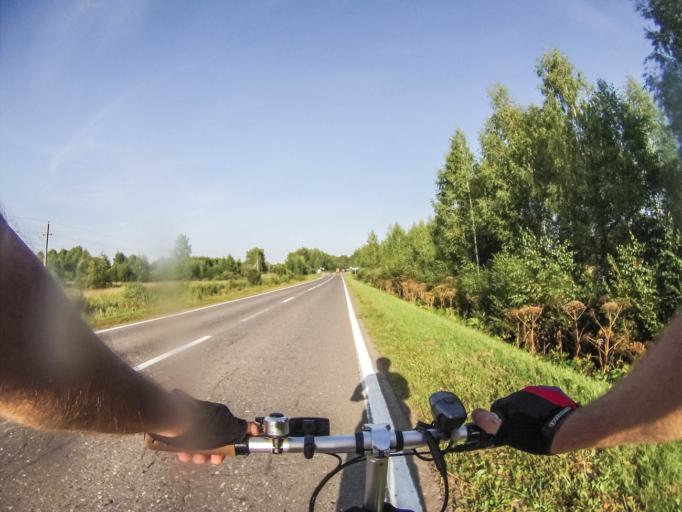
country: RU
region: Jaroslavl
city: Myshkin
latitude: 57.7138
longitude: 38.3875
